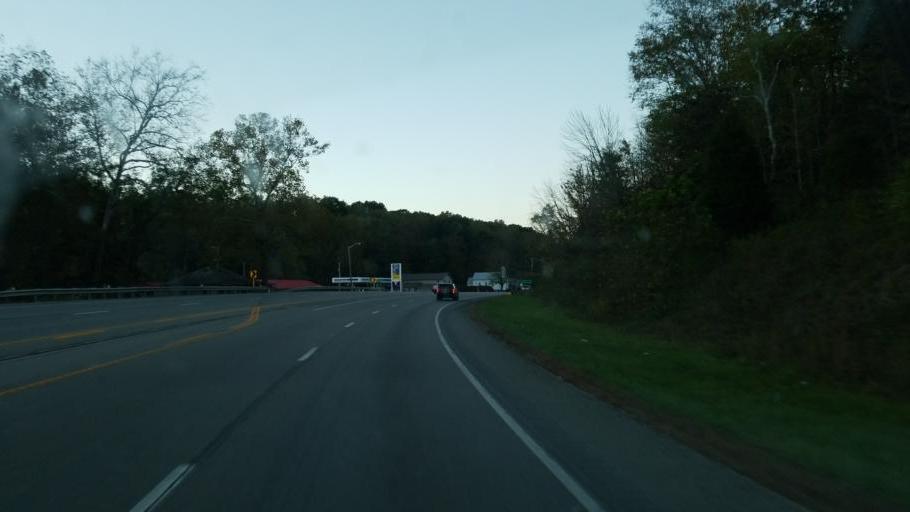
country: US
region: Ohio
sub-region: Pike County
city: Waverly
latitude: 39.1868
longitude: -82.9786
